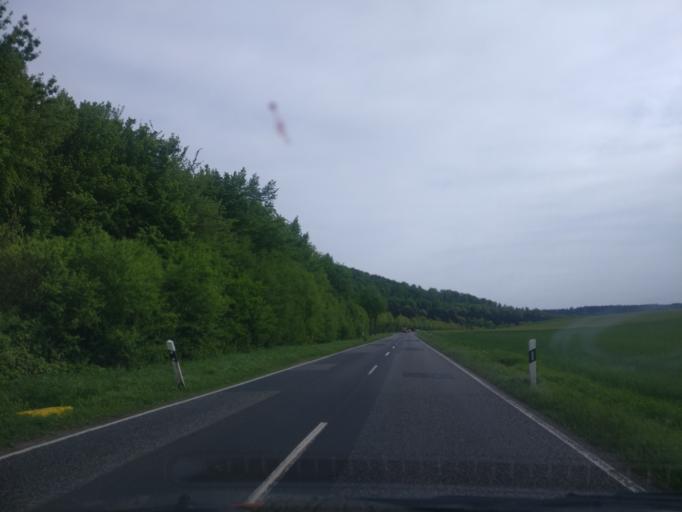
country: DE
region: Hesse
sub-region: Regierungsbezirk Kassel
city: Fuldatal
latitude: 51.3983
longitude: 9.5751
